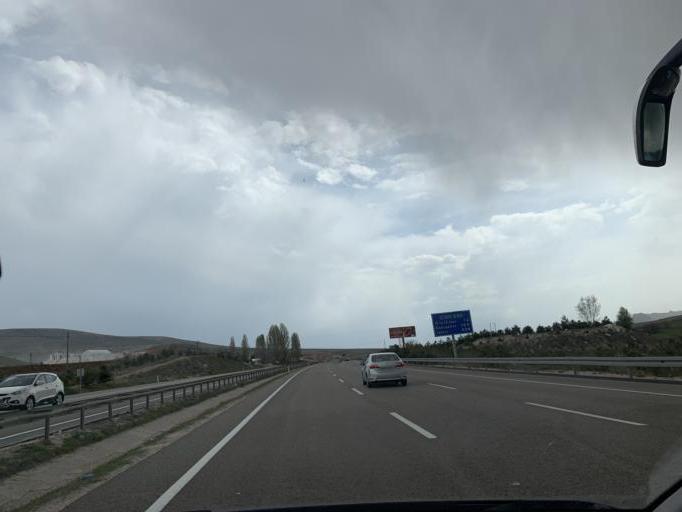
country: TR
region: Eskisehir
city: Sivrihisar
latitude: 39.4867
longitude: 31.5993
